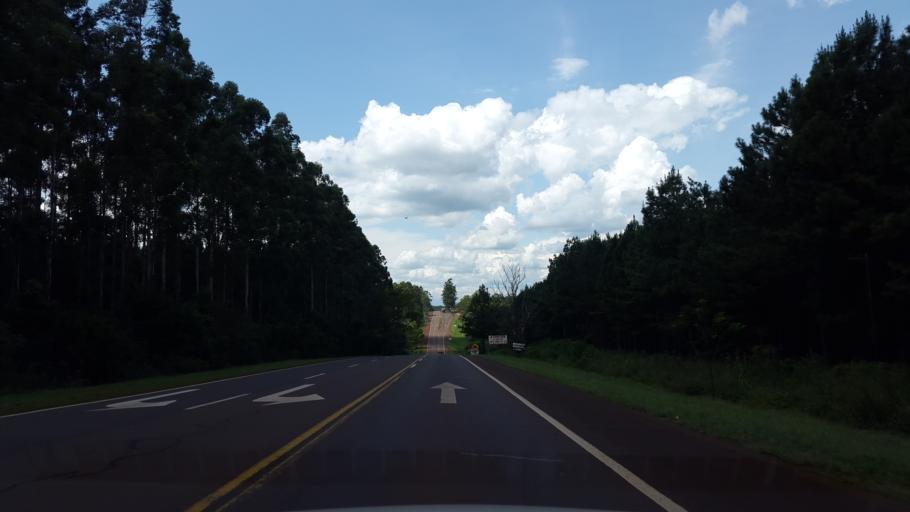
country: AR
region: Misiones
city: El Alcazar
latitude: -26.6923
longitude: -54.8278
